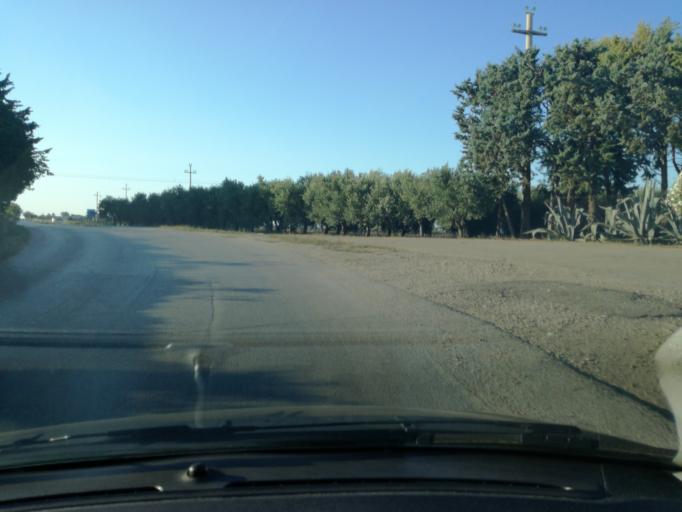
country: IT
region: Molise
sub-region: Provincia di Campobasso
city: San Giacomo degli Schiavoni
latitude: 41.9364
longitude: 14.9461
